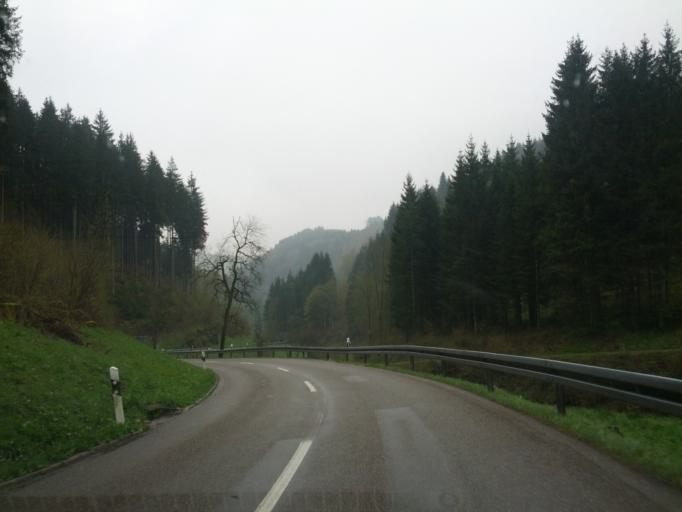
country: DE
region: Baden-Wuerttemberg
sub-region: Freiburg Region
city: Wieden
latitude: 47.8309
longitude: 7.8972
